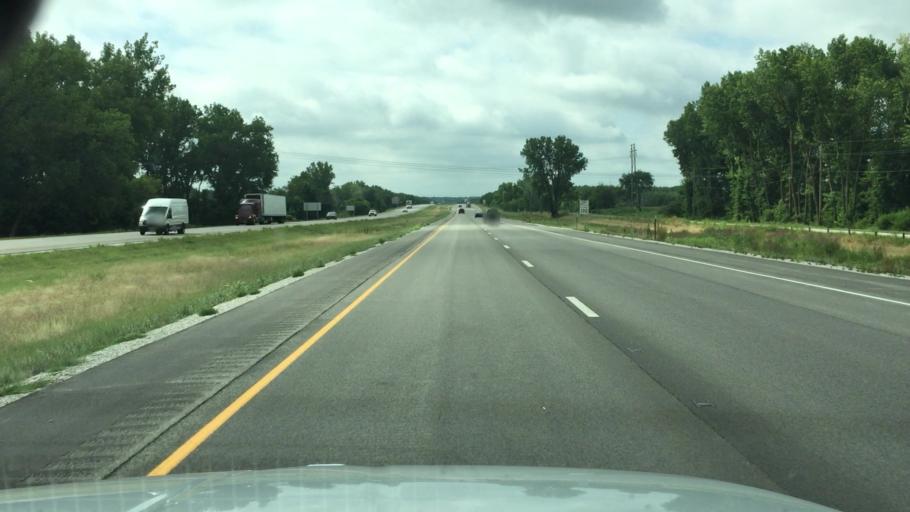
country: US
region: Illinois
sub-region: Henry County
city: Colona
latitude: 41.5297
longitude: -90.3417
